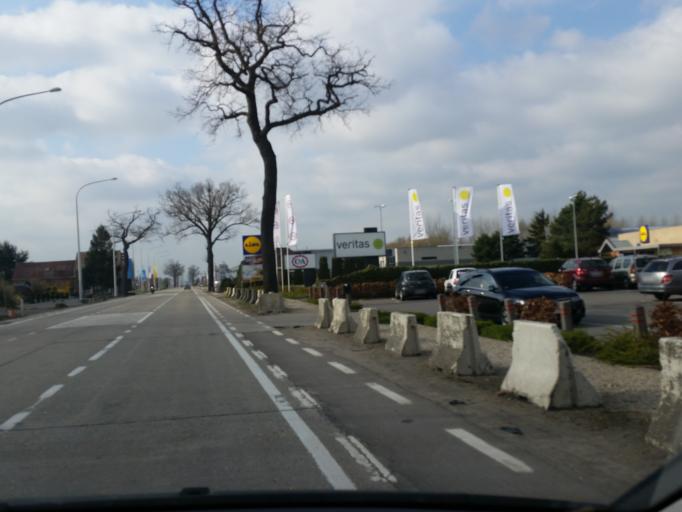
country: BE
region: Flanders
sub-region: Provincie Vlaams-Brabant
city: Boortmeerbeek
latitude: 50.9637
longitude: 4.5805
